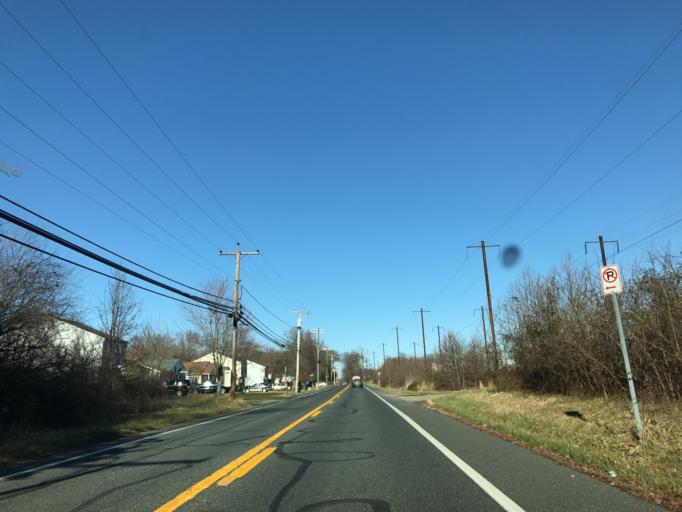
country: US
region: Maryland
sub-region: Harford County
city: Perryman
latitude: 39.4487
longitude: -76.2202
